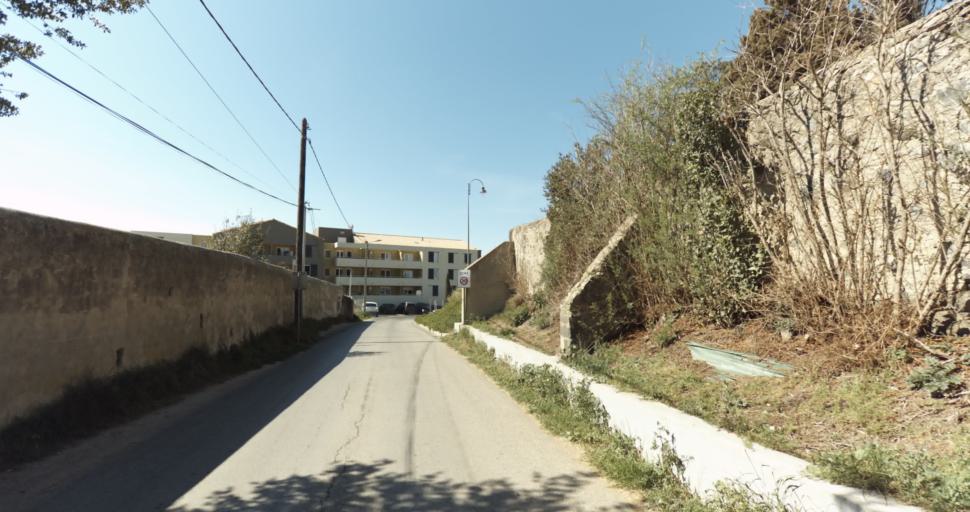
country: FR
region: Languedoc-Roussillon
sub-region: Departement de l'Herault
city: Marseillan
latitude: 43.3593
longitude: 3.5311
